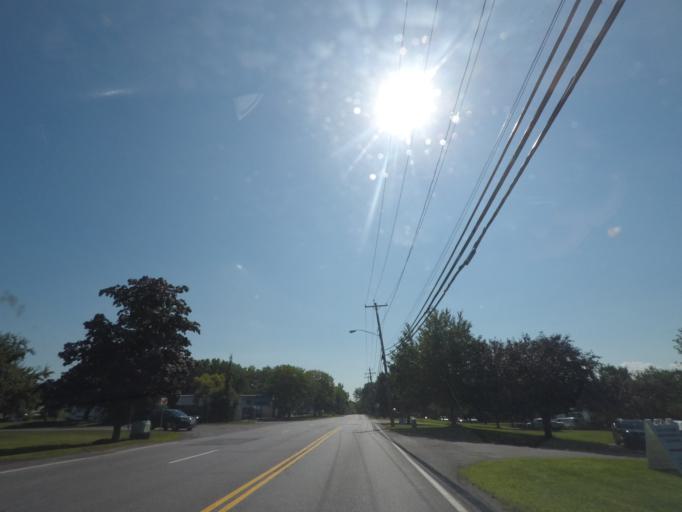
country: US
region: New York
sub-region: Albany County
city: Roessleville
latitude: 42.7535
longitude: -73.7786
